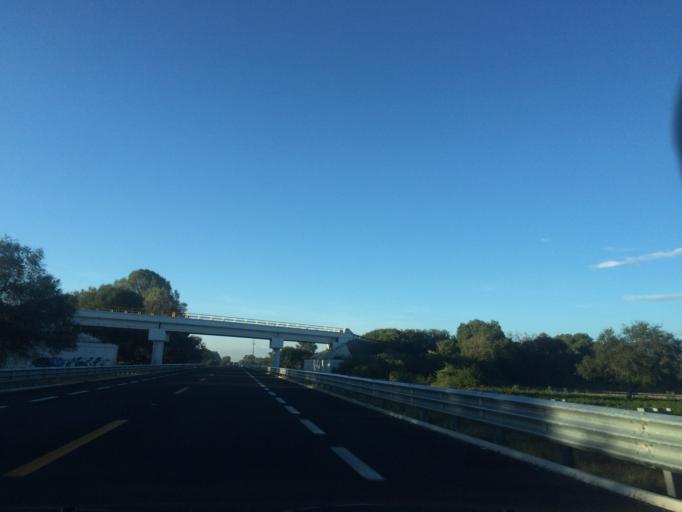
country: MX
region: Puebla
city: Santiago Miahuatlan
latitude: 18.5416
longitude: -97.4604
